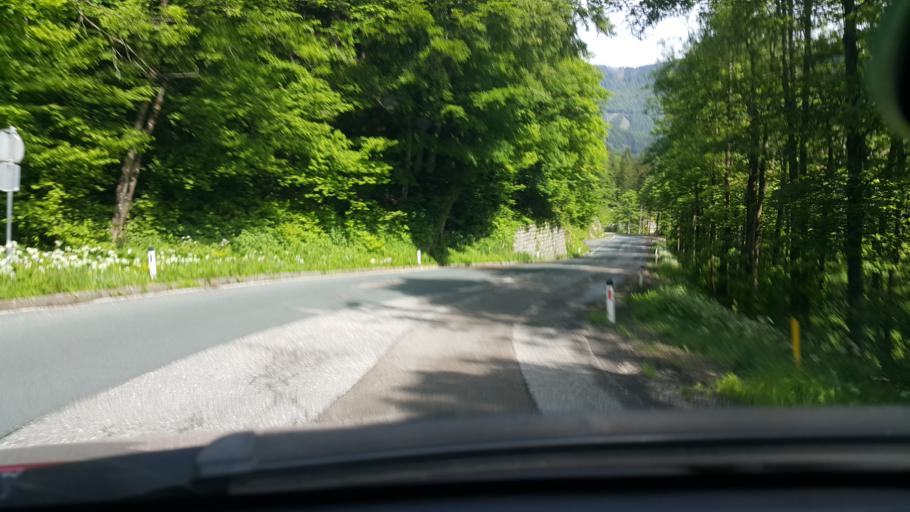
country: AT
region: Carinthia
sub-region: Politischer Bezirk Klagenfurt Land
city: Ferlach
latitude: 46.4619
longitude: 14.2579
